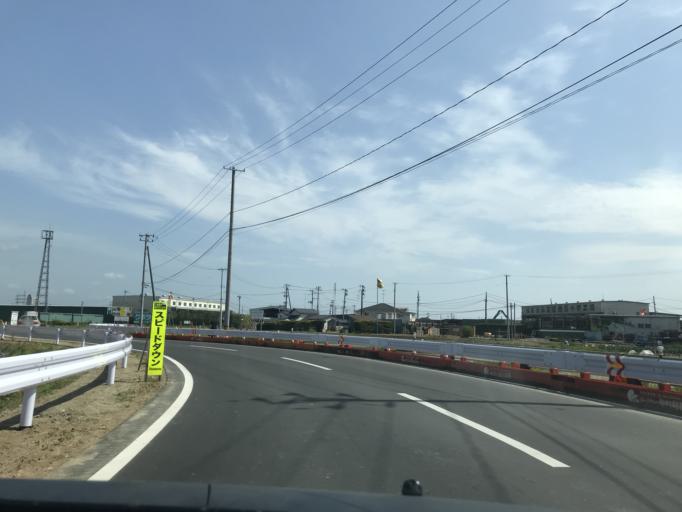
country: JP
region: Miyagi
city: Wakuya
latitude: 38.6999
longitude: 141.2020
